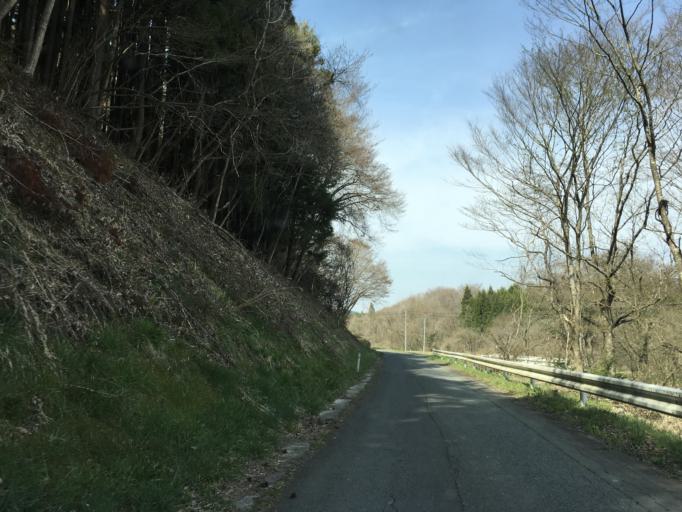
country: JP
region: Iwate
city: Ichinoseki
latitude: 38.8286
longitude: 141.3509
